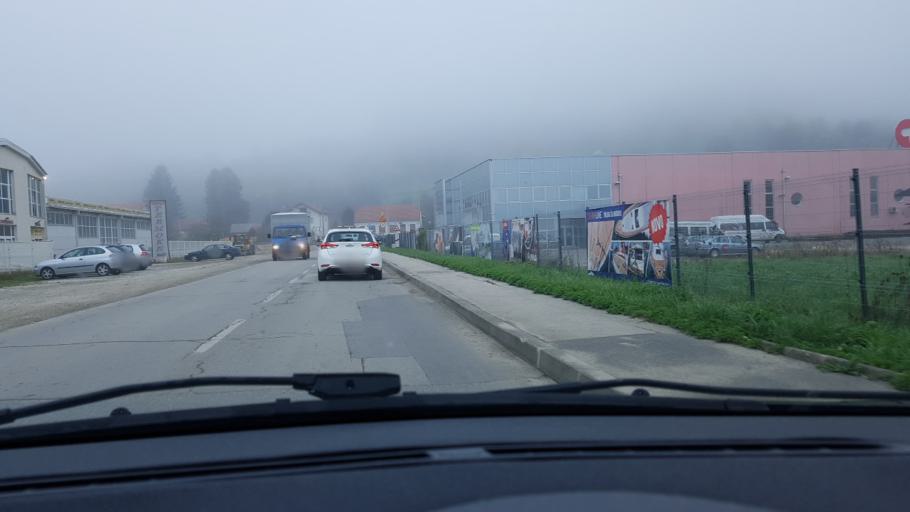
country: HR
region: Krapinsko-Zagorska
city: Zabok
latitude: 46.0180
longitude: 15.8915
